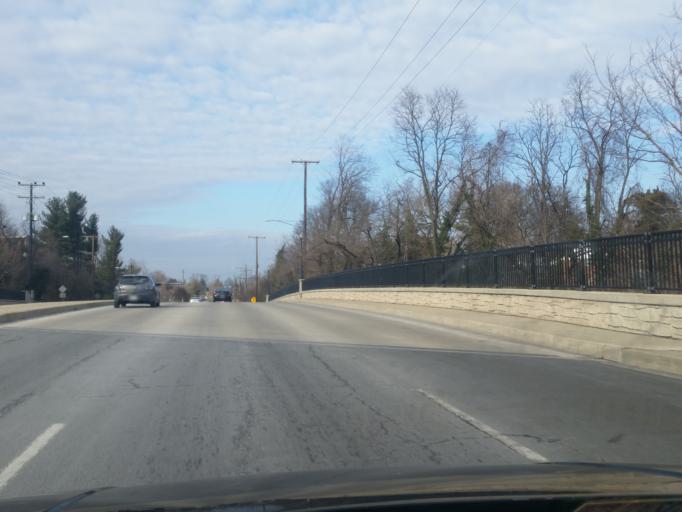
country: US
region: Maryland
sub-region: Montgomery County
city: Silver Spring
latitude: 38.9993
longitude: -77.0398
